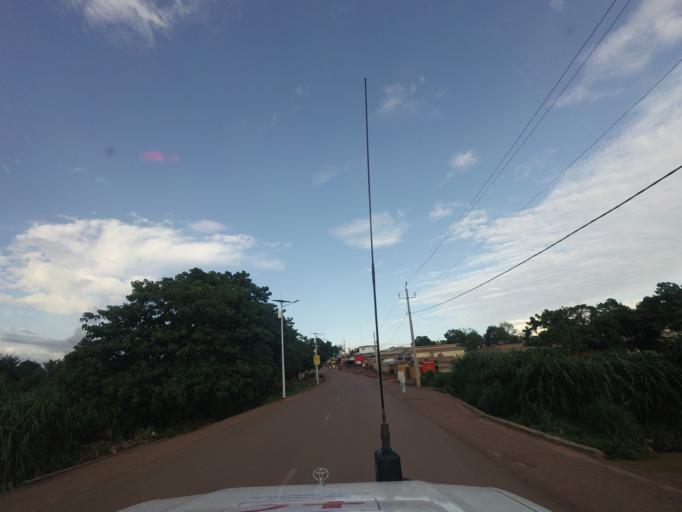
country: GN
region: Nzerekore
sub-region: Nzerekore Prefecture
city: Nzerekore
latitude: 7.7382
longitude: -8.8229
